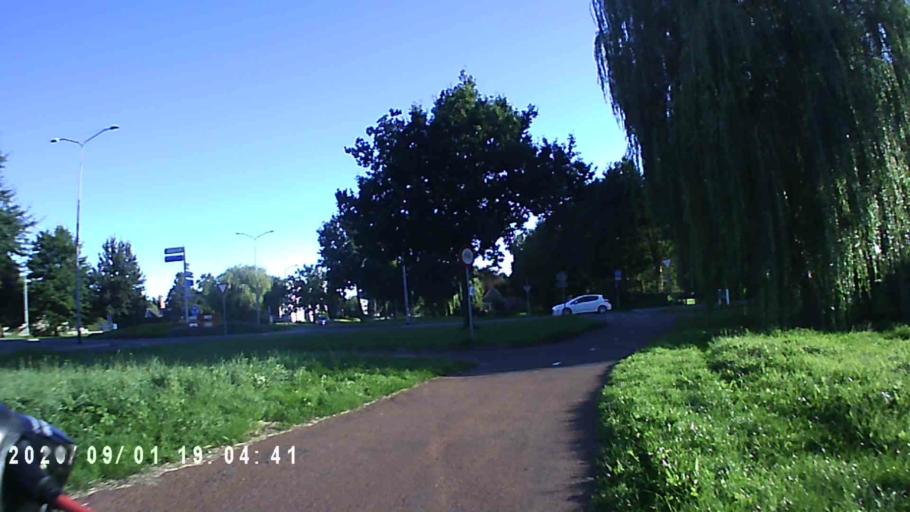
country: NL
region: Groningen
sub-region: Gemeente Veendam
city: Veendam
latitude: 53.1107
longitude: 6.8712
